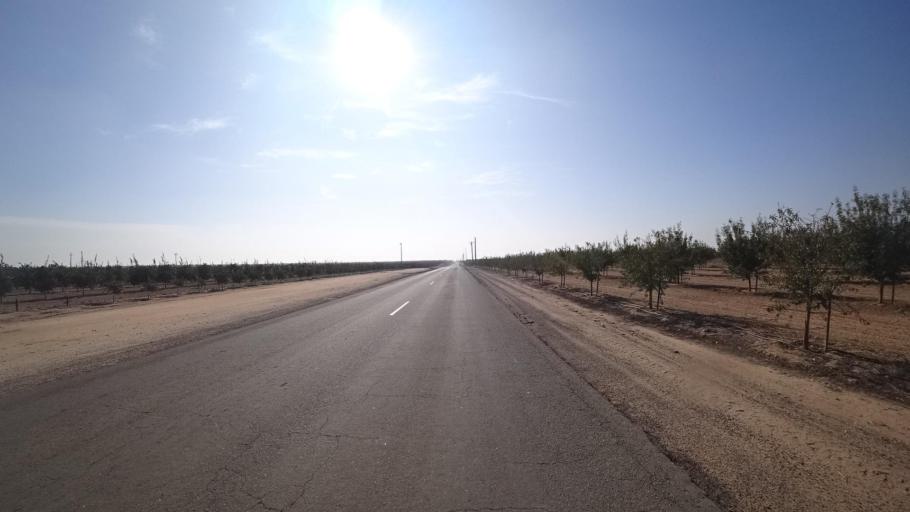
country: US
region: California
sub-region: Kern County
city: McFarland
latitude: 35.6542
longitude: -119.1690
